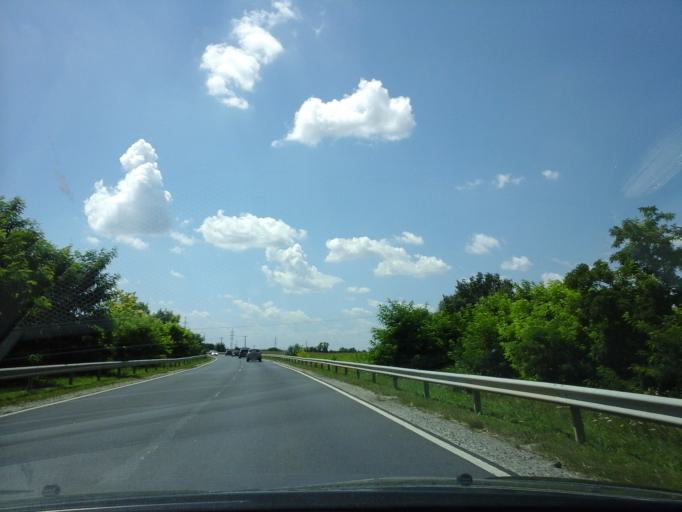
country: HU
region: Hajdu-Bihar
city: Ebes
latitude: 47.4654
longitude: 21.4540
